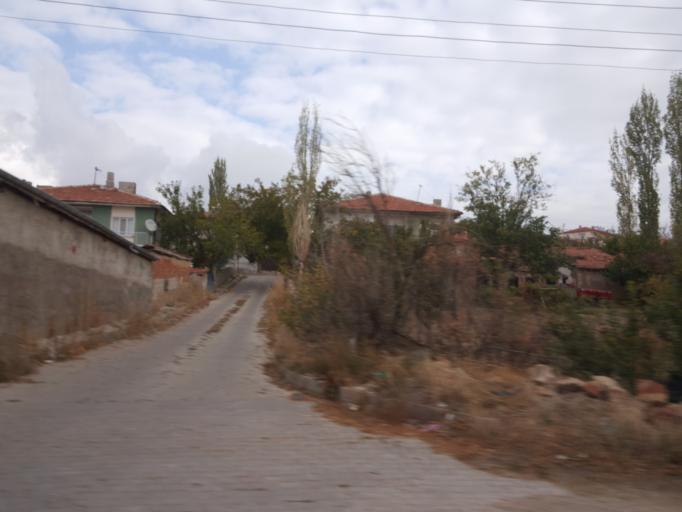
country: TR
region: Kirikkale
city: Keskin
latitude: 39.6728
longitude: 33.6071
